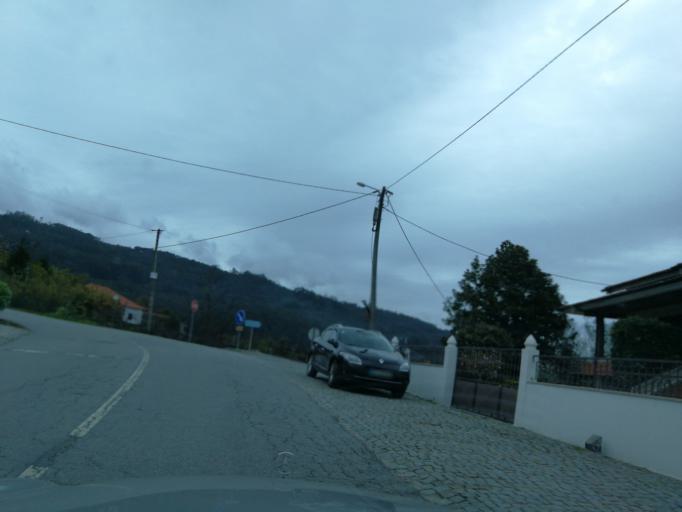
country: PT
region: Braga
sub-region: Braga
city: Oliveira
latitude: 41.4790
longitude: -8.4713
